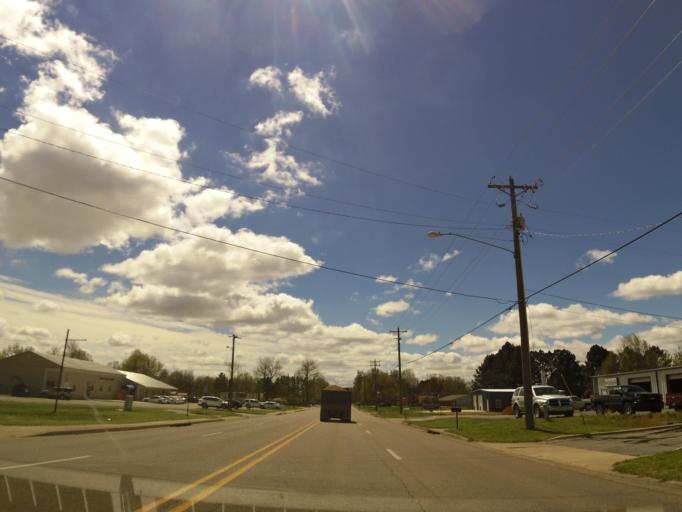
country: US
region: Arkansas
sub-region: Craighead County
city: Jonesboro
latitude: 35.8665
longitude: -90.7030
